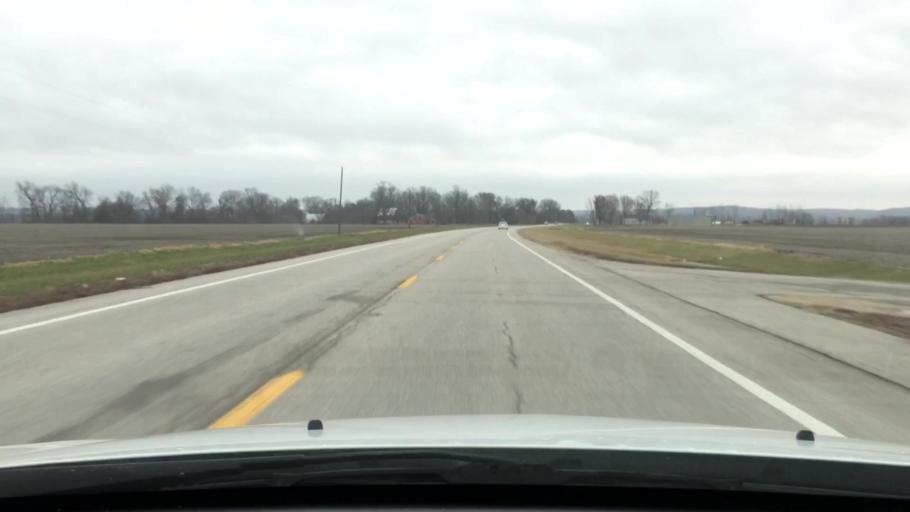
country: US
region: Missouri
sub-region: Pike County
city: Louisiana
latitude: 39.4834
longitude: -91.0152
